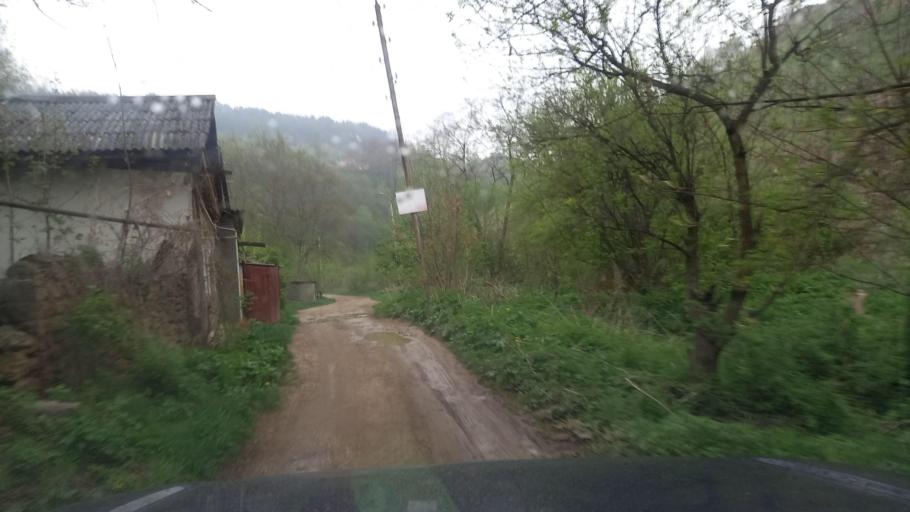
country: RU
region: Stavropol'skiy
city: Kislovodsk
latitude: 43.8909
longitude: 42.7071
